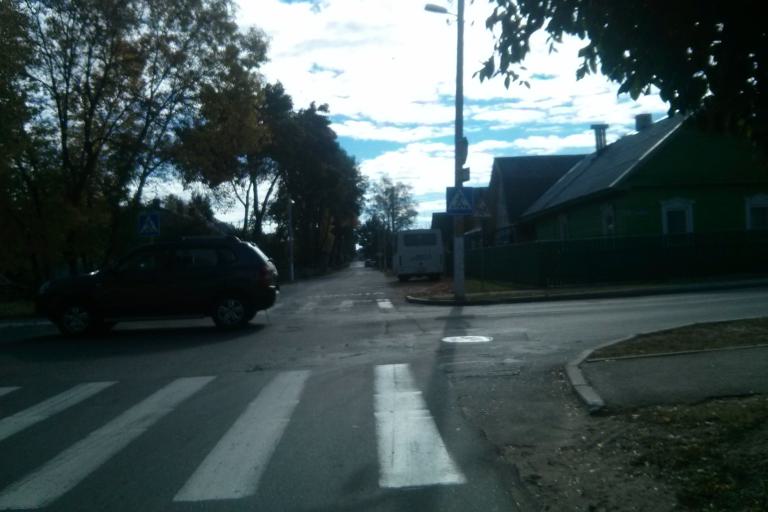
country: BY
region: Minsk
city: Chervyen'
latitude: 53.7117
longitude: 28.4202
